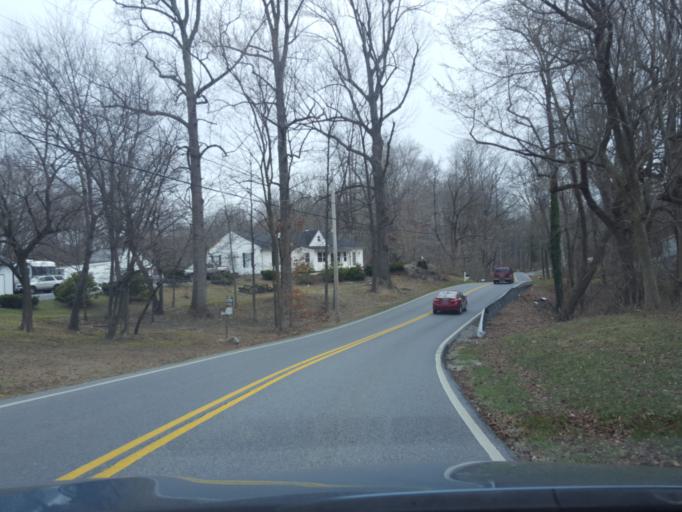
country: US
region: Maryland
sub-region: Calvert County
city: North Beach
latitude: 38.7148
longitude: -76.5611
